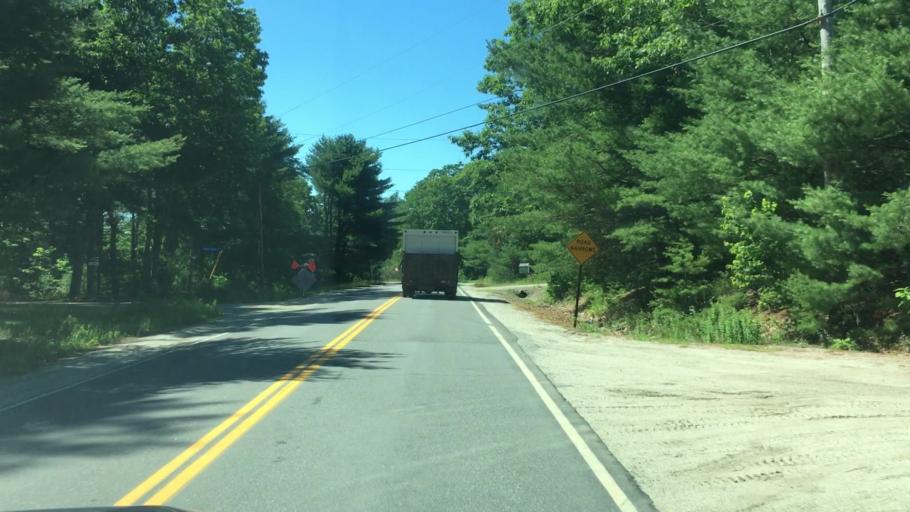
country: US
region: Maine
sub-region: Hancock County
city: Sedgwick
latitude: 44.3492
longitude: -68.5874
